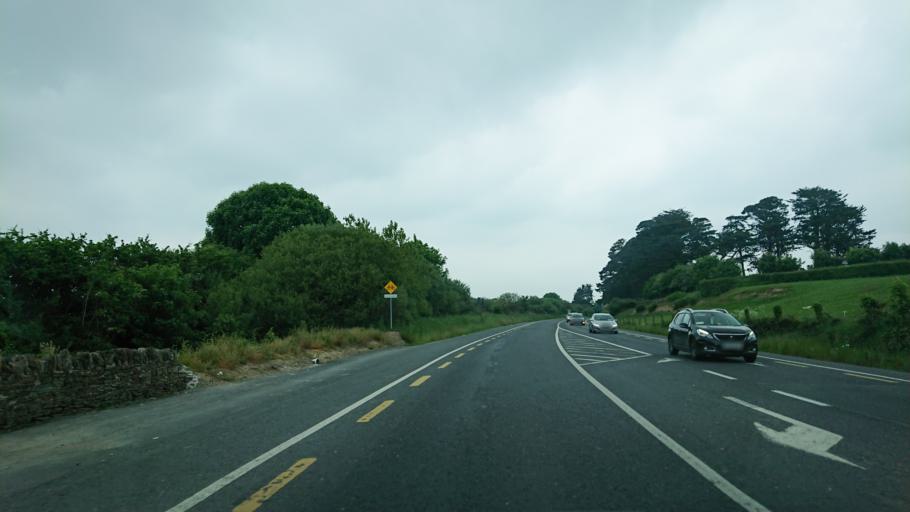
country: IE
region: Munster
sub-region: Waterford
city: Tra Mhor
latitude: 52.1927
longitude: -7.1255
